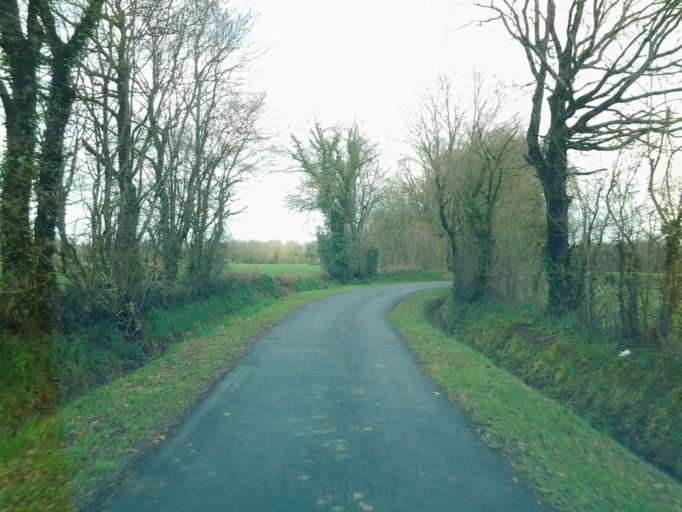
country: FR
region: Pays de la Loire
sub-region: Departement de la Vendee
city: La Chaize-le-Vicomte
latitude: 46.6604
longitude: -1.3448
